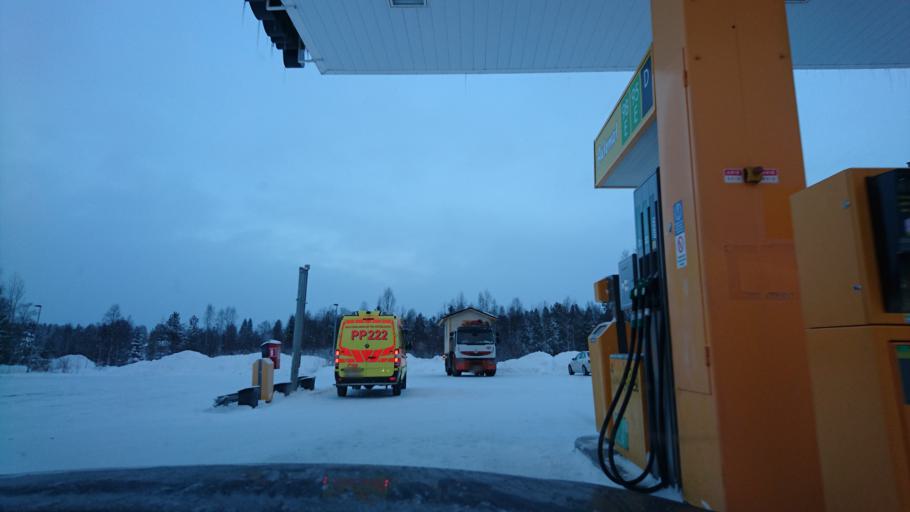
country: FI
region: Northern Ostrobothnia
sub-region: Koillismaa
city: Taivalkoski
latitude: 65.5709
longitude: 28.2444
